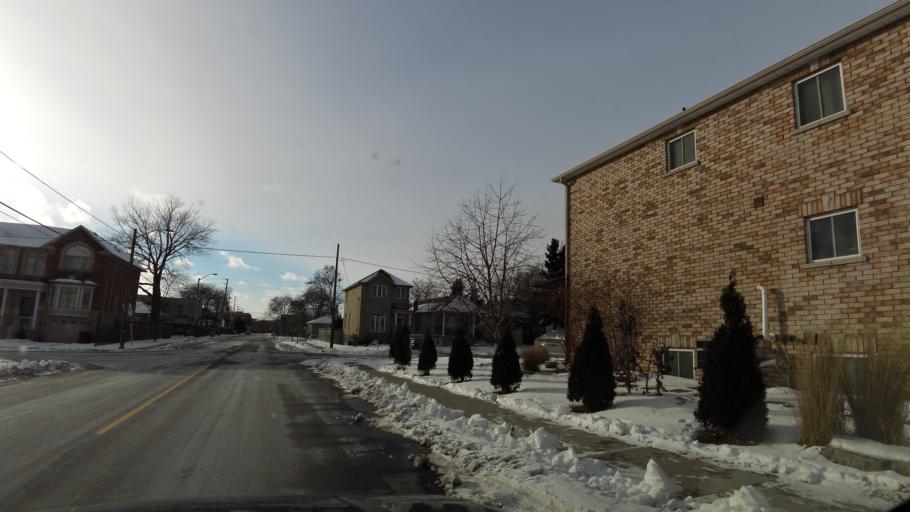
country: CA
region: Ontario
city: Etobicoke
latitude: 43.5982
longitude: -79.5293
